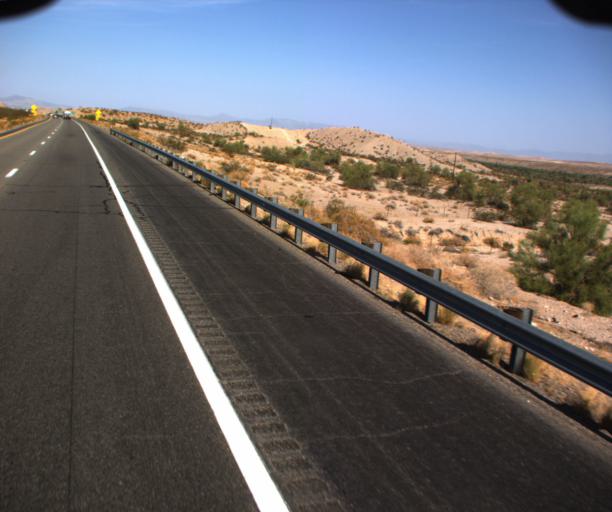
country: US
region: Arizona
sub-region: Mohave County
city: Desert Hills
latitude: 34.7272
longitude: -114.3909
